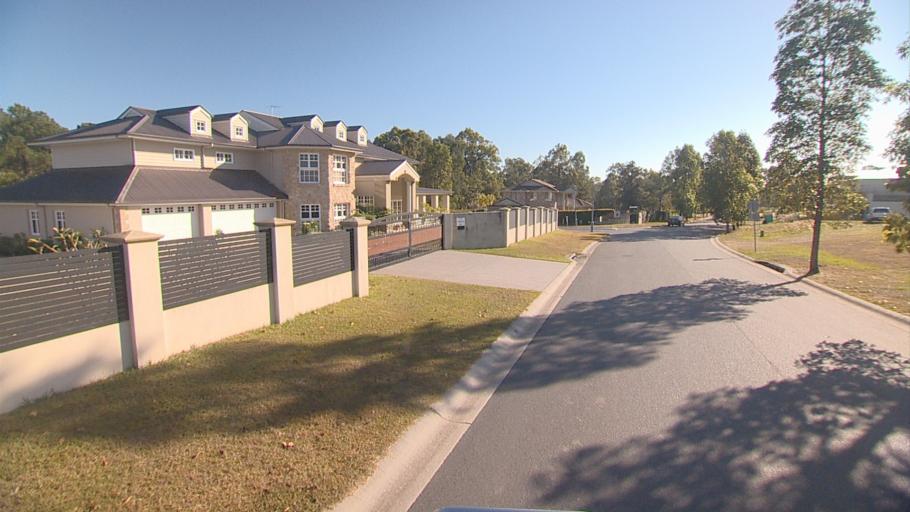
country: AU
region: Queensland
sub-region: Brisbane
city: Forest Lake
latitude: -27.6564
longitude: 152.9923
